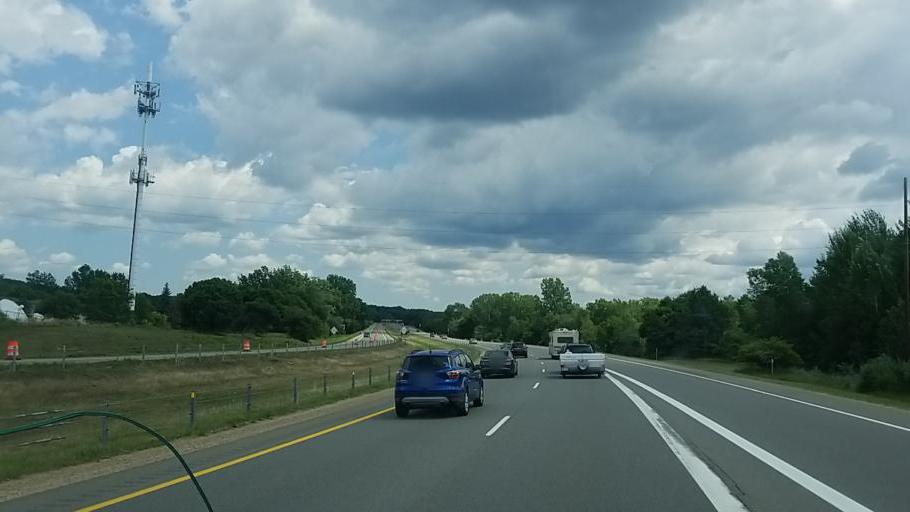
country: US
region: Michigan
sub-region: Kent County
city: Comstock Park
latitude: 43.0177
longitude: -85.6333
